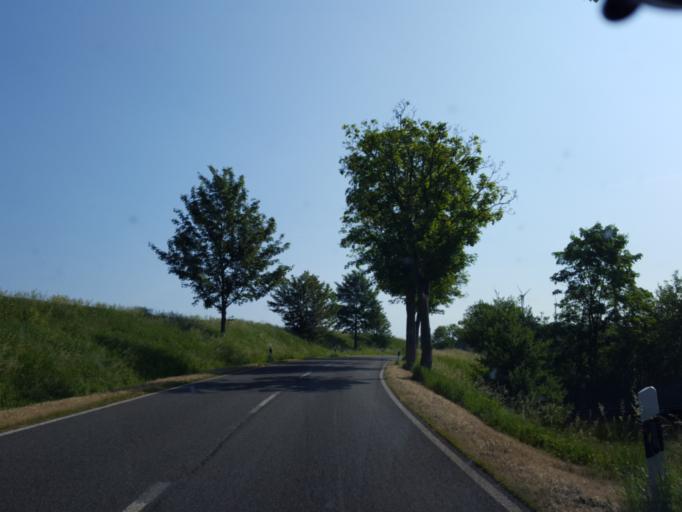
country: DE
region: Lower Saxony
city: Wulften
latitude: 51.6627
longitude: 10.1873
